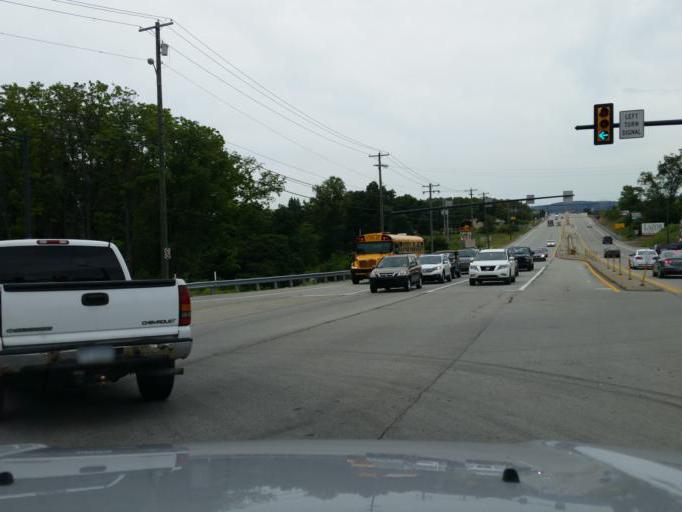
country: US
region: Pennsylvania
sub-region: Westmoreland County
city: Lawson Heights
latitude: 40.2829
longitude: -79.4047
